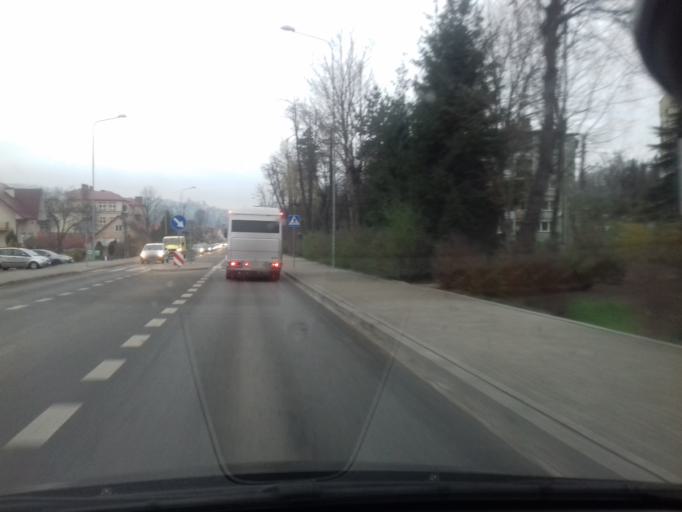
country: PL
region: Lesser Poland Voivodeship
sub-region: Powiat limanowski
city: Limanowa
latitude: 49.7192
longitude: 20.4099
